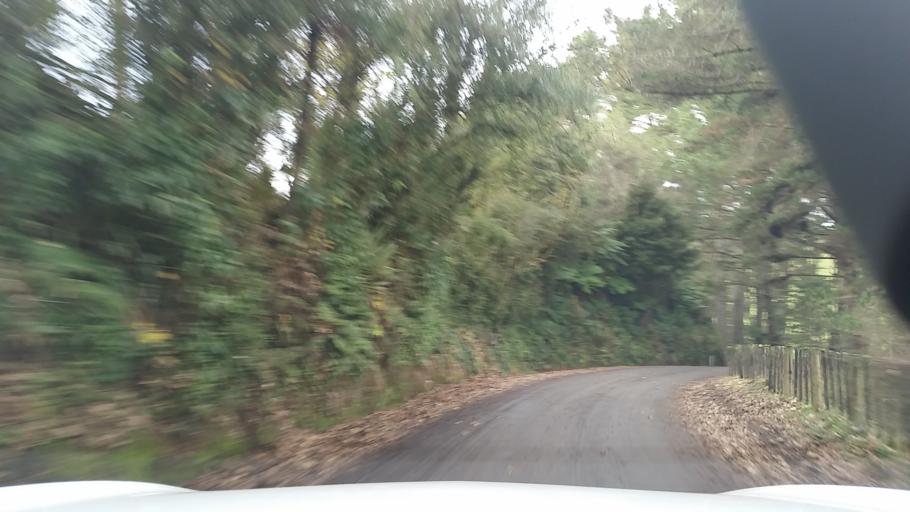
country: NZ
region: Taranaki
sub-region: New Plymouth District
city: Waitara
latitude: -39.1493
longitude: 174.5080
